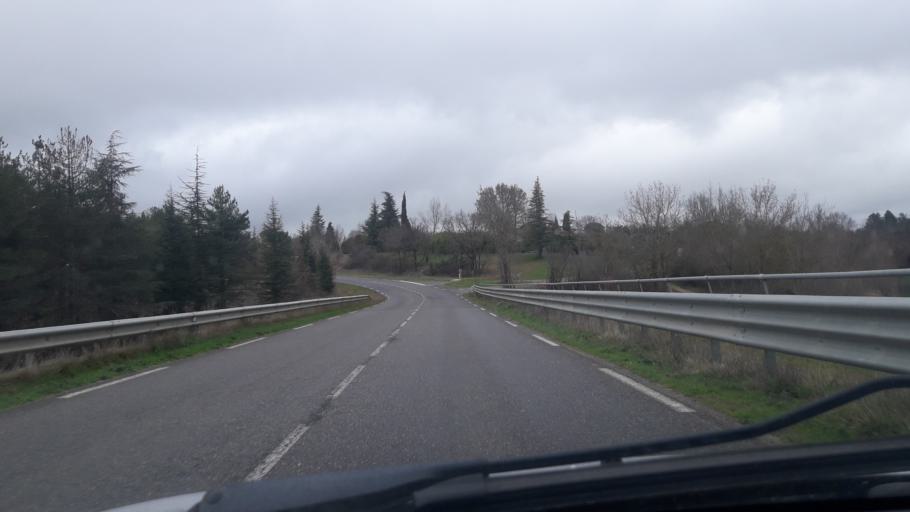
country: FR
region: Midi-Pyrenees
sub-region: Departement du Gers
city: Gimont
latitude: 43.6907
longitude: 0.9984
